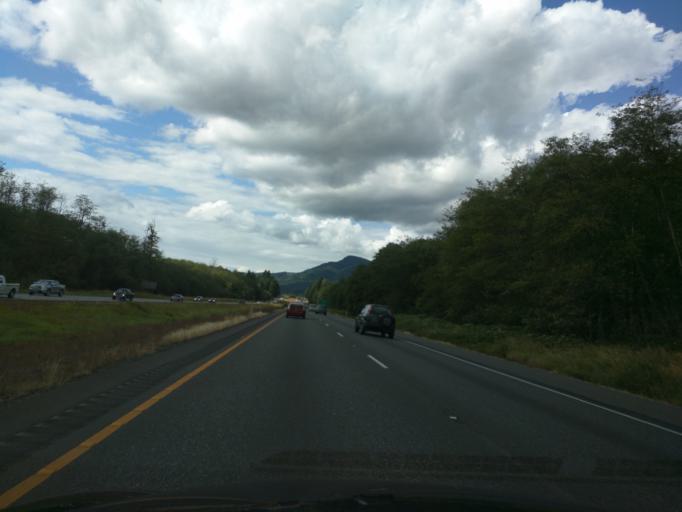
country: US
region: Washington
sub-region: Whatcom County
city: Sudden Valley
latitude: 48.6364
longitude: -122.3608
